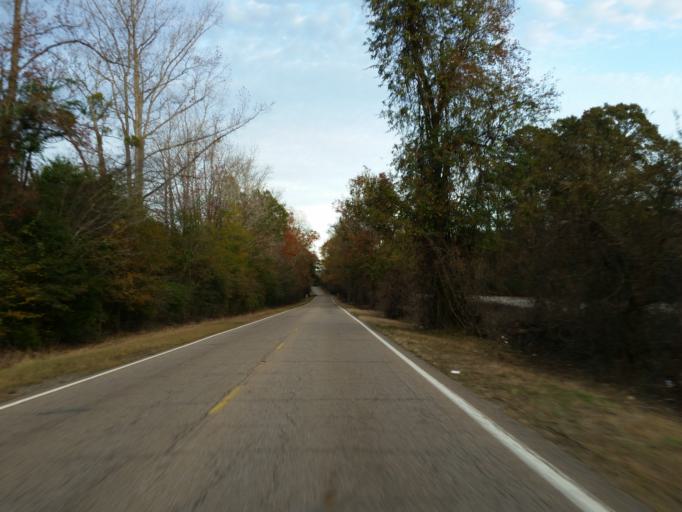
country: US
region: Alabama
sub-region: Sumter County
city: York
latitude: 32.4239
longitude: -88.4292
